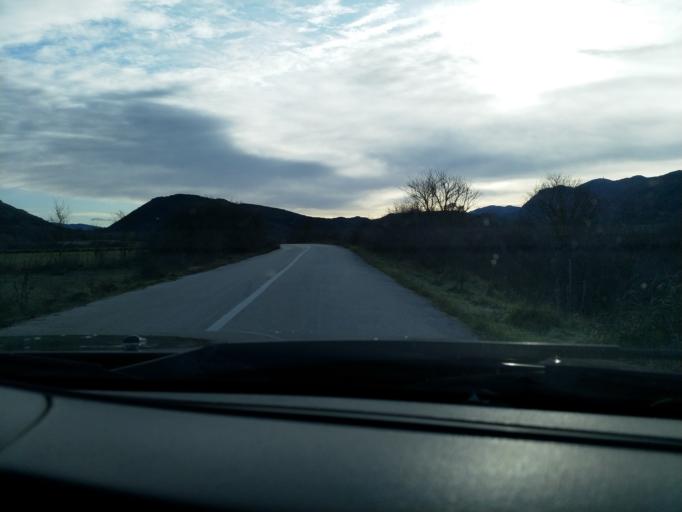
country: GR
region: Epirus
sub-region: Nomos Ioanninon
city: Asprangeloi
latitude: 39.8689
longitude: 20.7069
